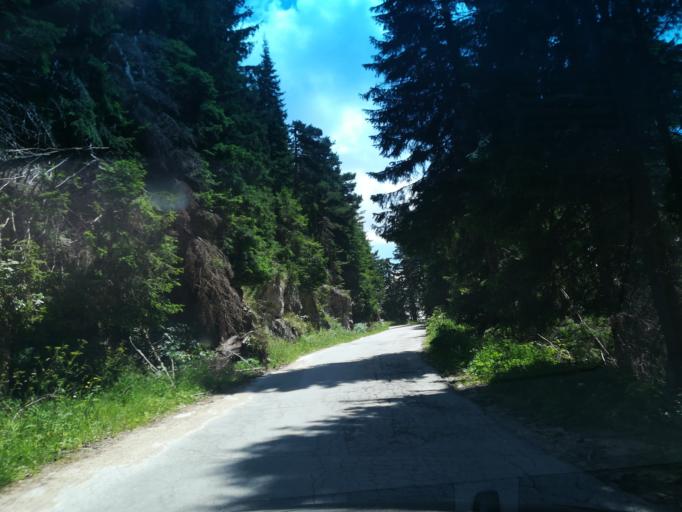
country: BG
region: Smolyan
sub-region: Obshtina Chepelare
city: Chepelare
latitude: 41.6934
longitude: 24.7766
